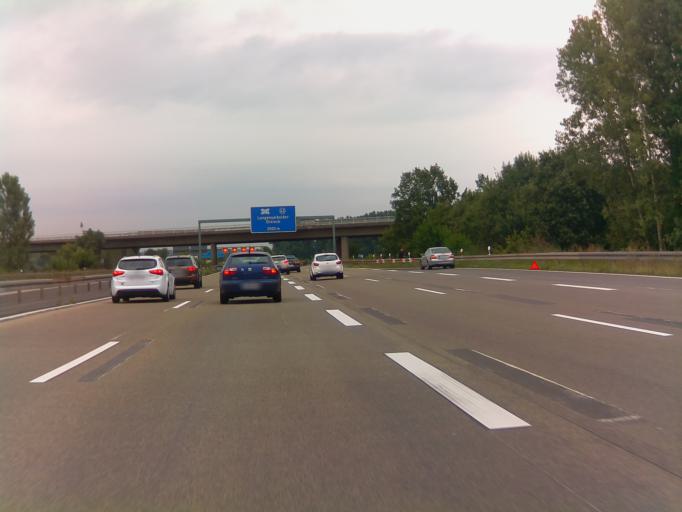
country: DE
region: Hesse
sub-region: Regierungsbezirk Darmstadt
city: Erlensee
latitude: 50.1464
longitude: 8.9987
